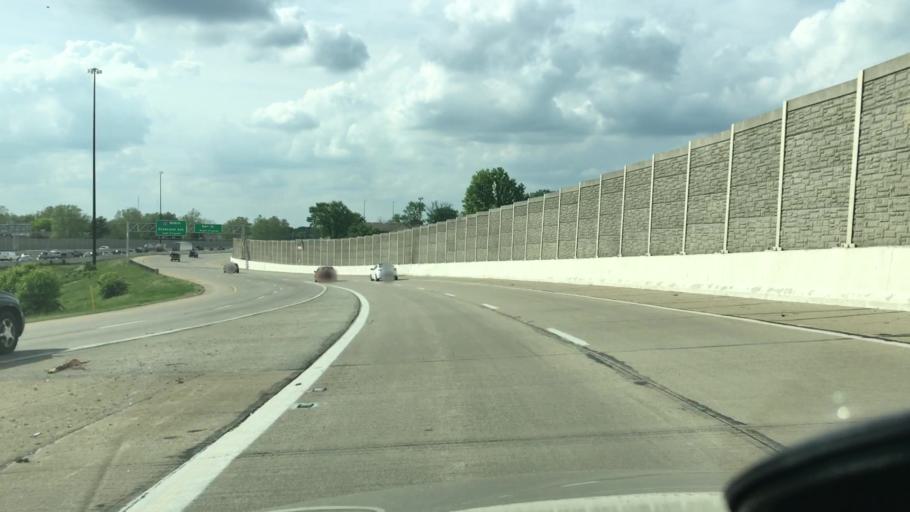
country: US
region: Indiana
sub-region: Marion County
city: Lawrence
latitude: 39.8484
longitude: -86.0437
